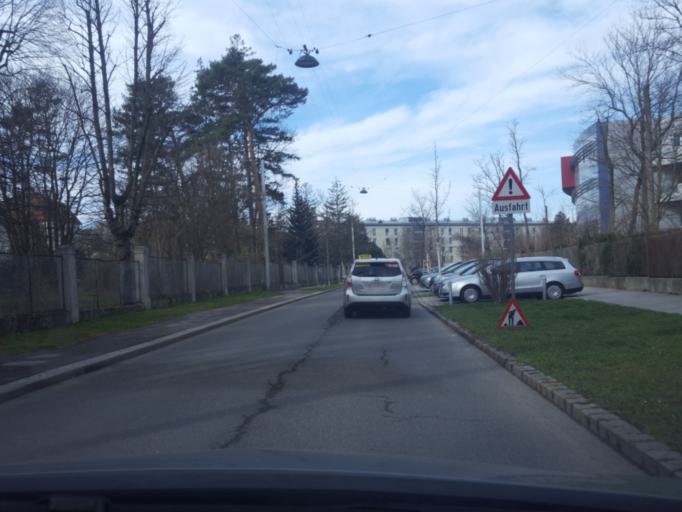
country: AT
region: Lower Austria
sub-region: Politischer Bezirk Modling
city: Perchtoldsdorf
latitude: 48.1626
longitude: 16.2830
